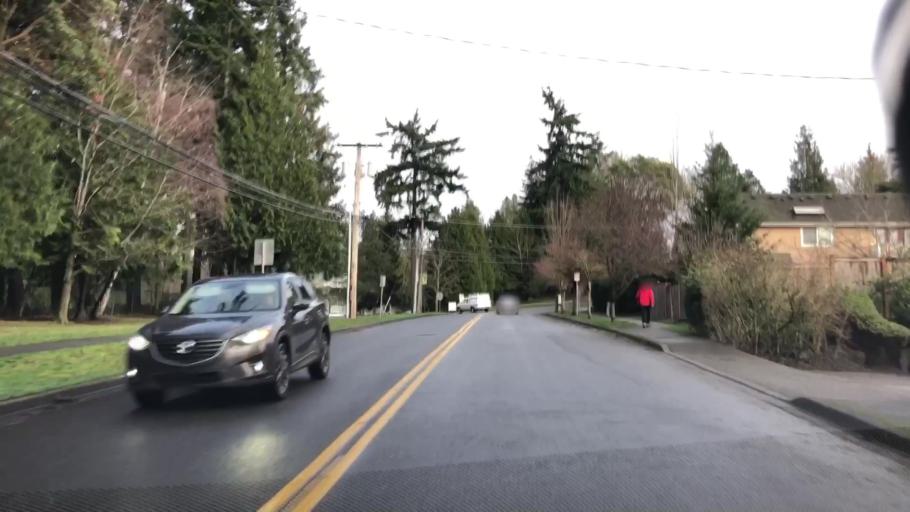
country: US
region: Washington
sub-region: King County
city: Yarrow Point
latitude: 47.6558
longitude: -122.1927
